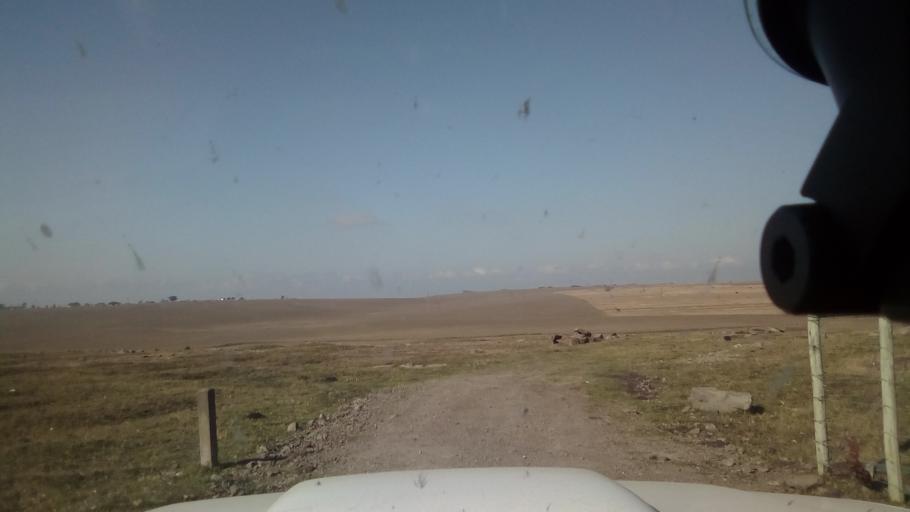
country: ZA
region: Eastern Cape
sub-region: Buffalo City Metropolitan Municipality
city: Bhisho
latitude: -32.9536
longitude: 27.3187
